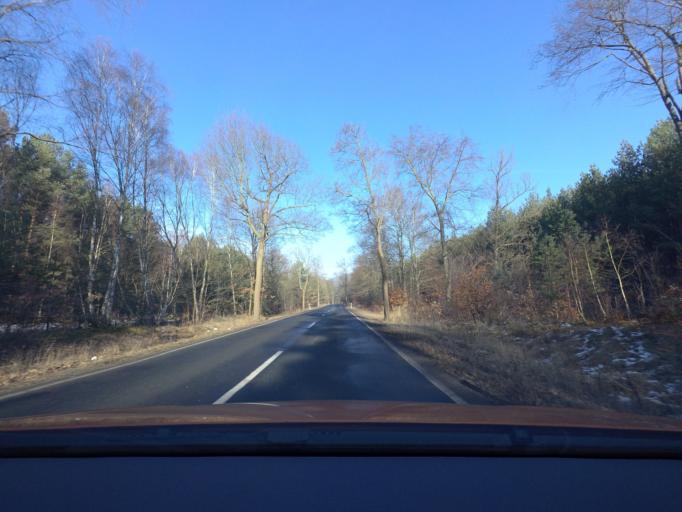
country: DE
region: Brandenburg
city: Wandlitz
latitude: 52.7276
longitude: 13.3680
